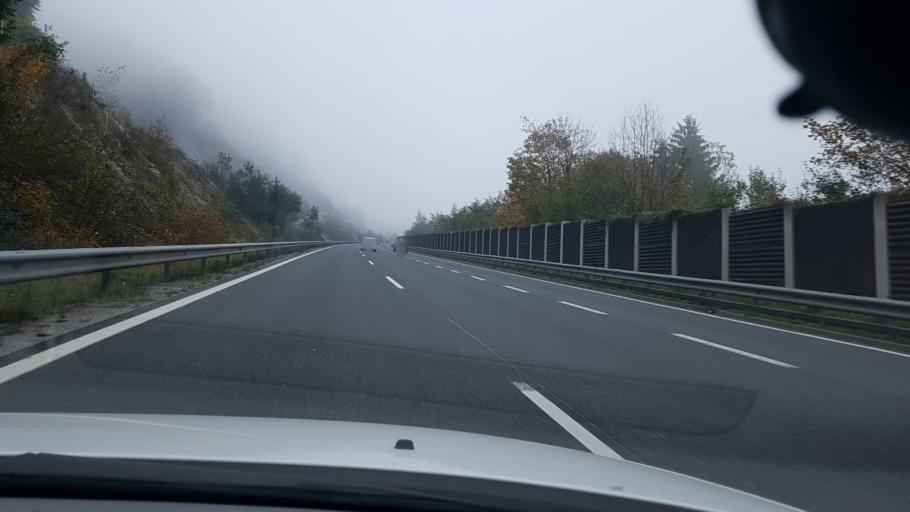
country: SI
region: Grosuplje
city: Grosuplje
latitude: 45.9621
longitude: 14.7332
